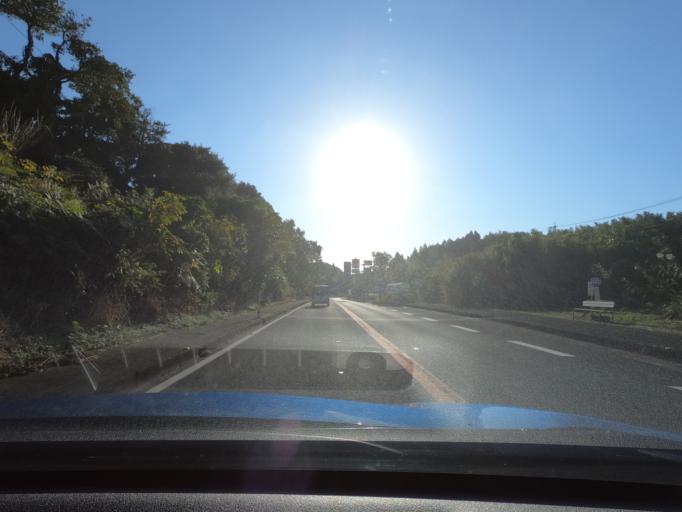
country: JP
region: Kagoshima
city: Akune
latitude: 32.0479
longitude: 130.2199
